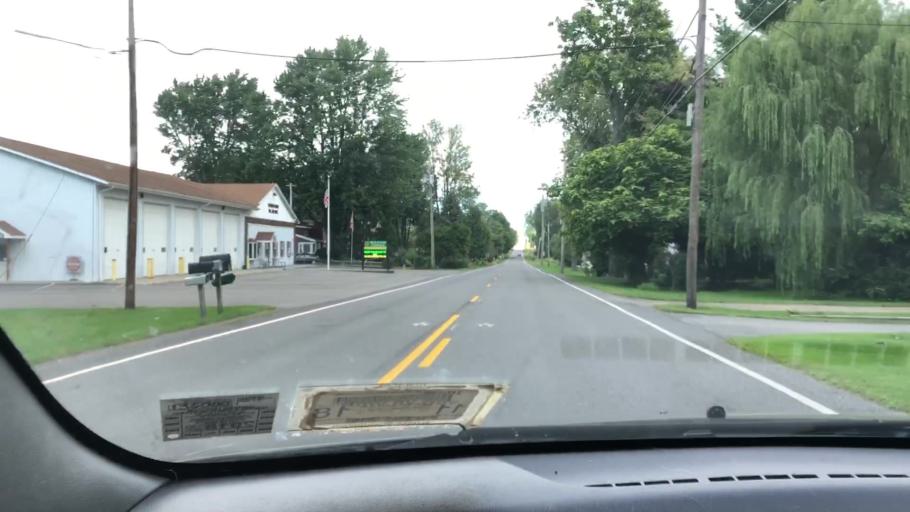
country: US
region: New York
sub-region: Wayne County
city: Macedon
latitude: 43.0956
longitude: -77.3205
